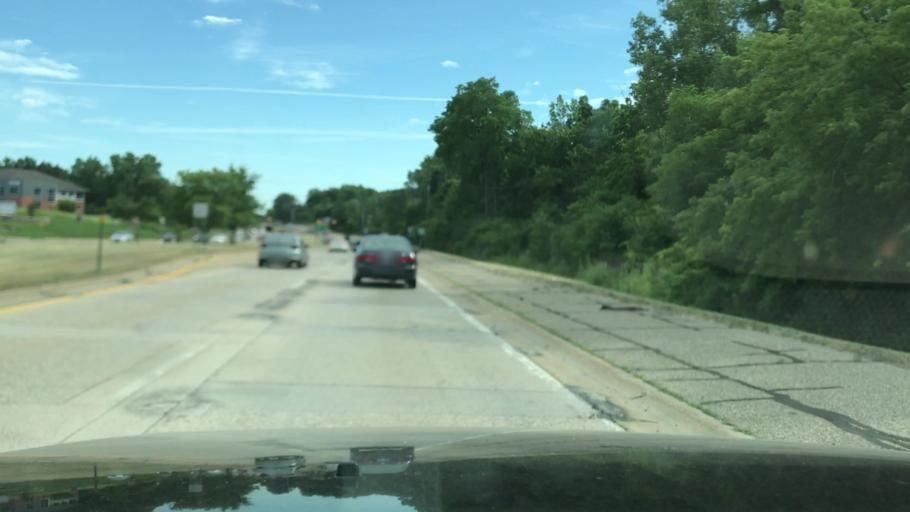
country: US
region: Michigan
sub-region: Kent County
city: East Grand Rapids
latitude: 42.9409
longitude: -85.5852
